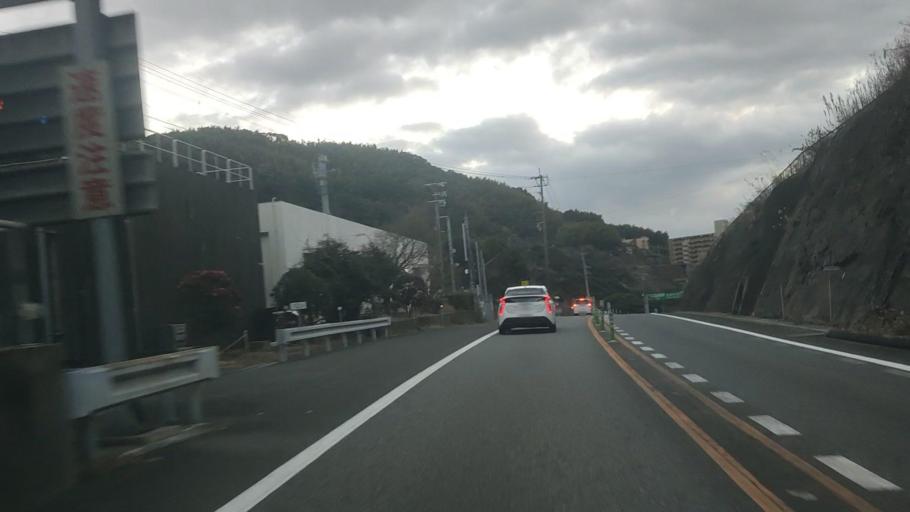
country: JP
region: Nagasaki
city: Nagasaki-shi
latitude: 32.7712
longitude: 129.8909
